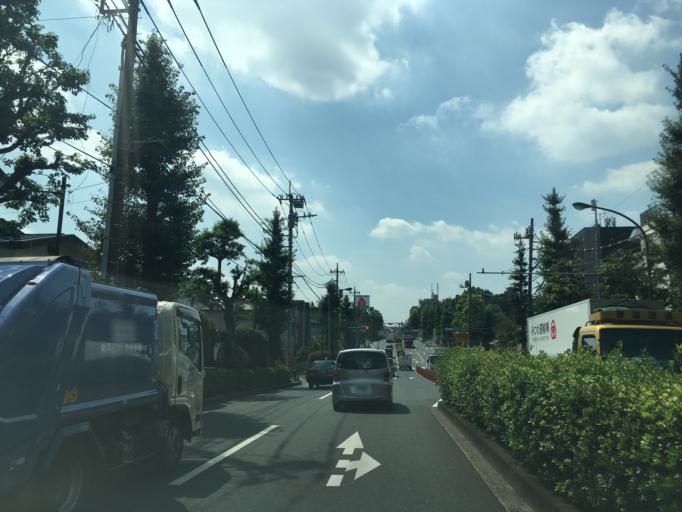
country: JP
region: Saitama
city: Wako
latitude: 35.7407
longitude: 139.6153
